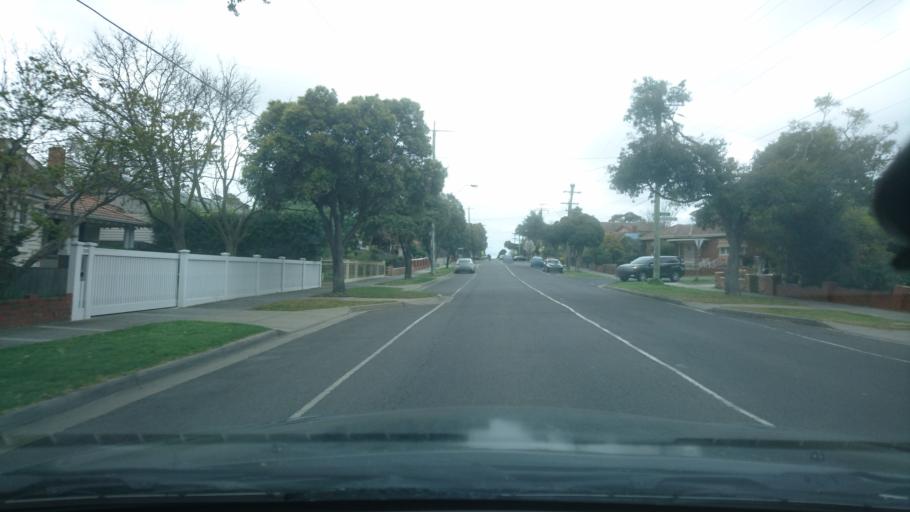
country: AU
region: Victoria
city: Hughesdale
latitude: -37.9009
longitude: 145.0756
